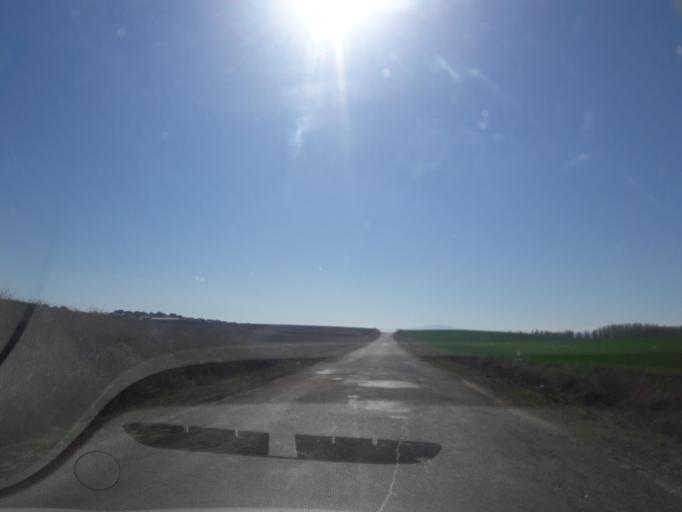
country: ES
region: Castille and Leon
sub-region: Provincia de Salamanca
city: Mancera de Abajo
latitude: 40.8259
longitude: -5.1810
